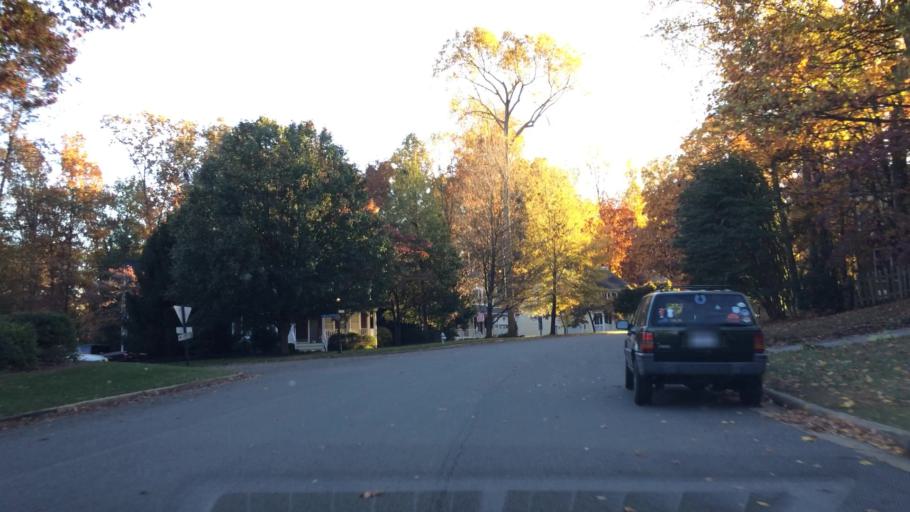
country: US
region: Virginia
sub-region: Henrico County
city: Chamberlayne
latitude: 37.6881
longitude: -77.4175
